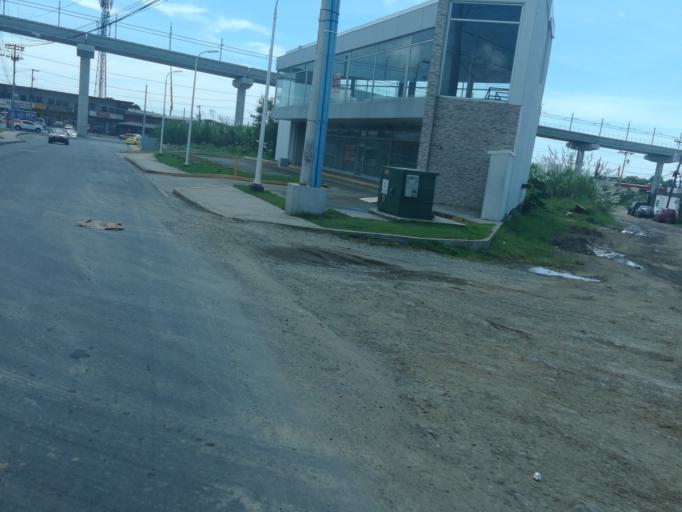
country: PA
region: Panama
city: Tocumen
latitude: 9.0854
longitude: -79.3990
